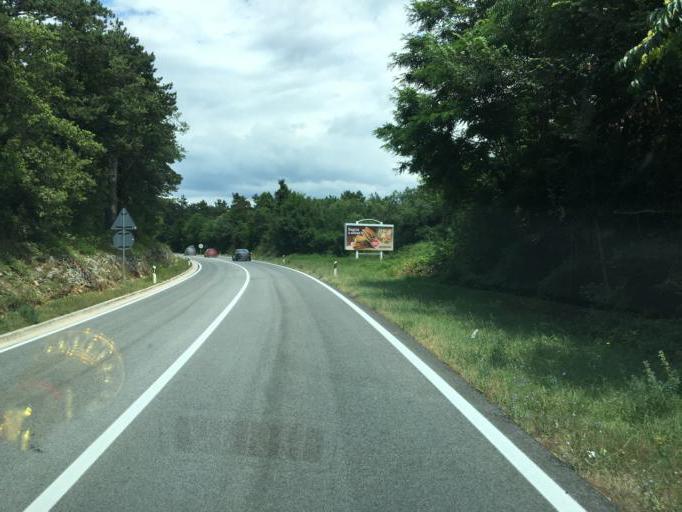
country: HR
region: Istarska
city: Karojba
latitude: 45.2234
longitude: 13.8393
